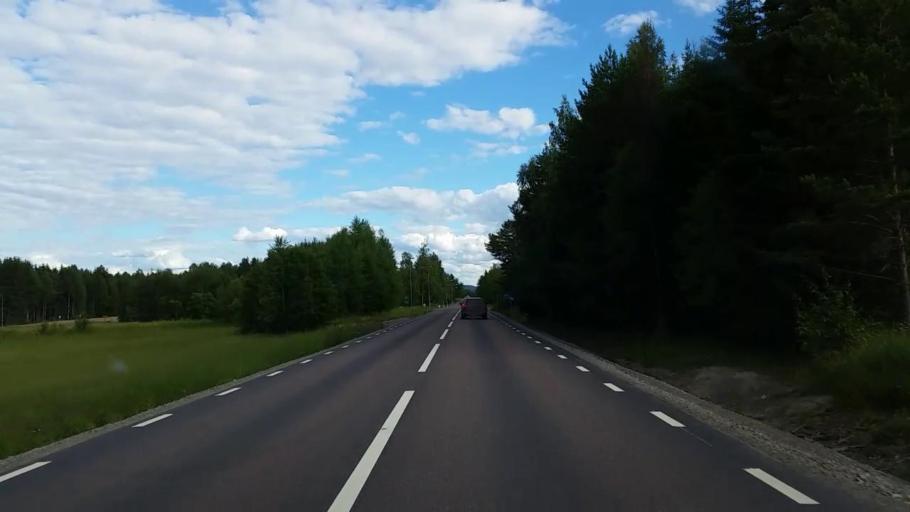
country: SE
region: Gaevleborg
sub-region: Ljusdals Kommun
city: Ljusdal
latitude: 61.8592
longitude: 15.9870
